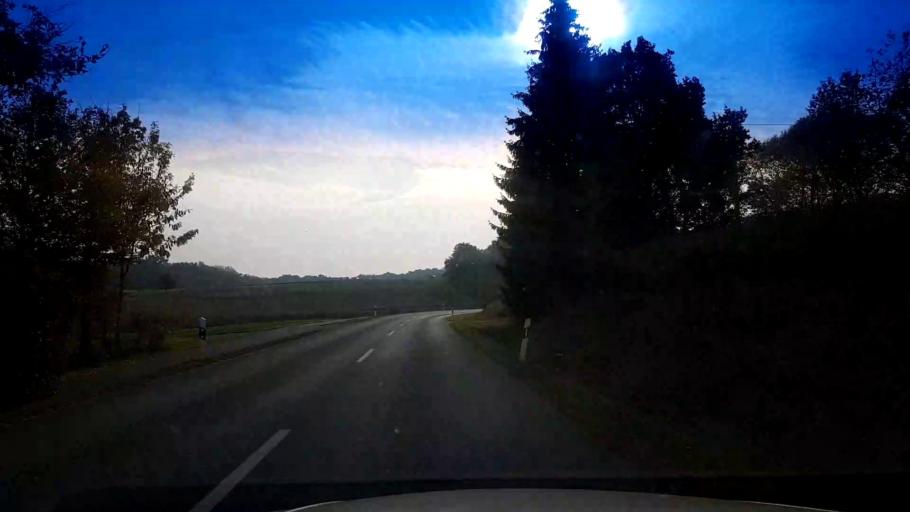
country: DE
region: Bavaria
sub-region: Upper Franconia
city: Altenkunstadt
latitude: 50.1227
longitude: 11.2599
